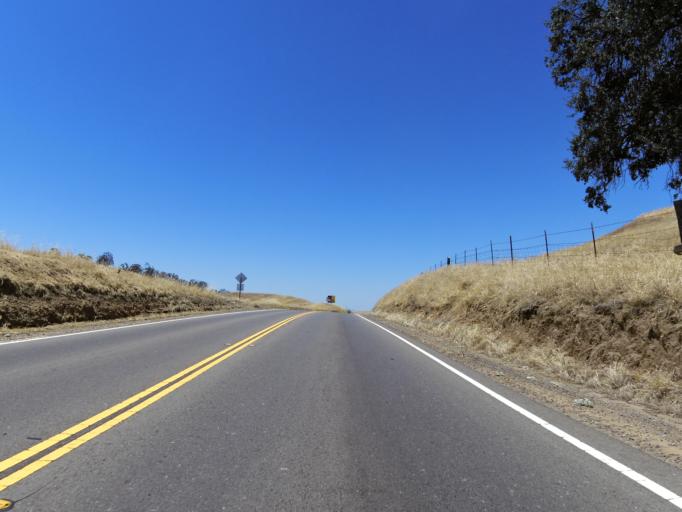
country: US
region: California
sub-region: Fresno County
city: Clovis
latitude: 36.9851
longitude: -119.6654
